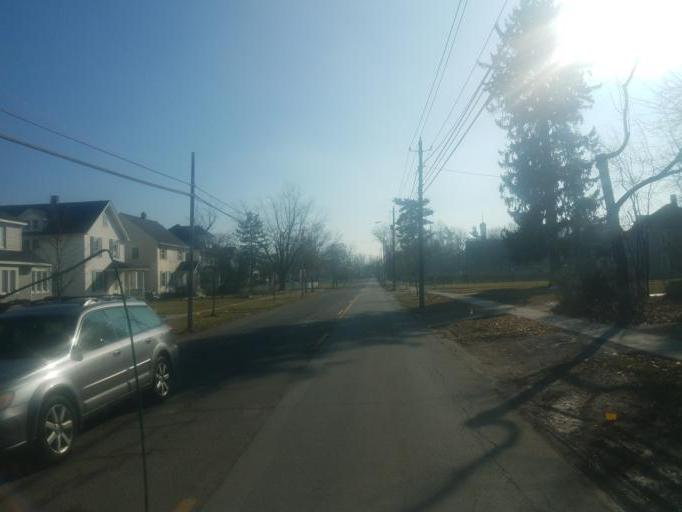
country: US
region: Ohio
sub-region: Seneca County
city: Tiffin
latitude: 41.1037
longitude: -83.1698
